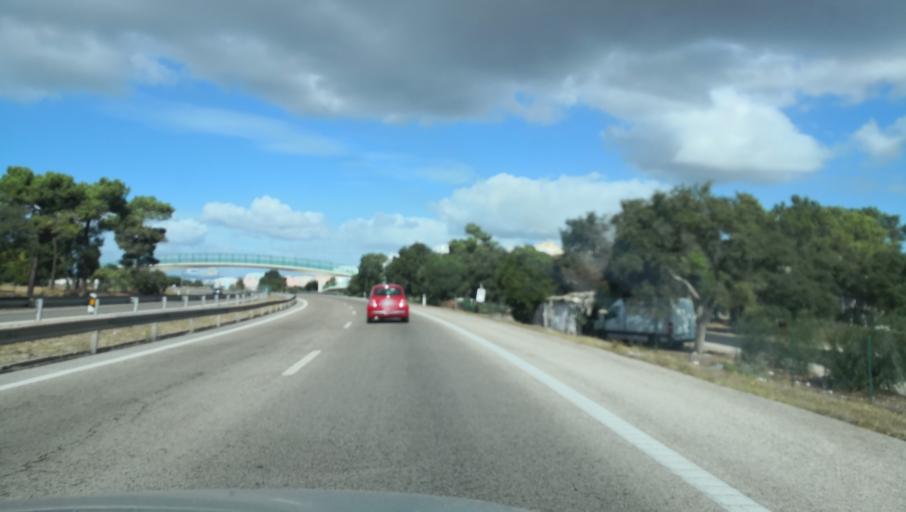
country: PT
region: Setubal
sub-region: Moita
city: Alhos Vedros
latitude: 38.6460
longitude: -9.0490
